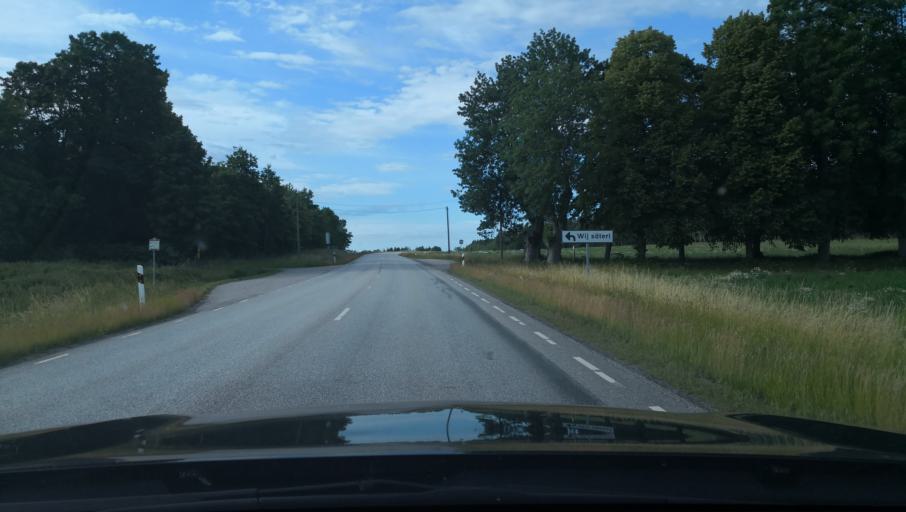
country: SE
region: Uppsala
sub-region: Habo Kommun
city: Balsta
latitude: 59.6165
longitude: 17.4991
